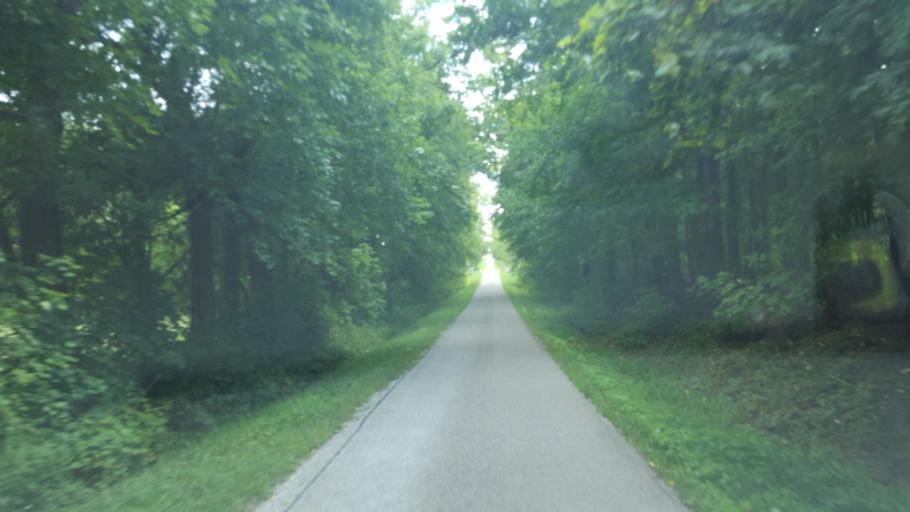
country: US
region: Ohio
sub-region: Huron County
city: Willard
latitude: 41.1164
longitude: -82.8254
